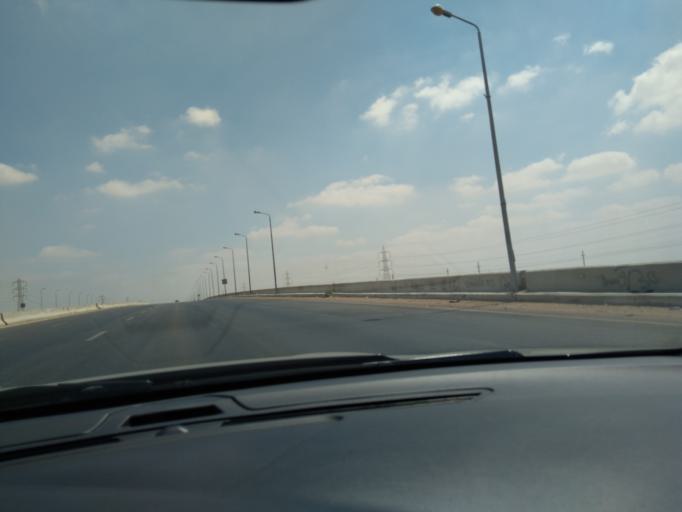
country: EG
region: Al Isma'iliyah
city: At Tall al Kabir
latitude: 30.3666
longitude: 31.9172
